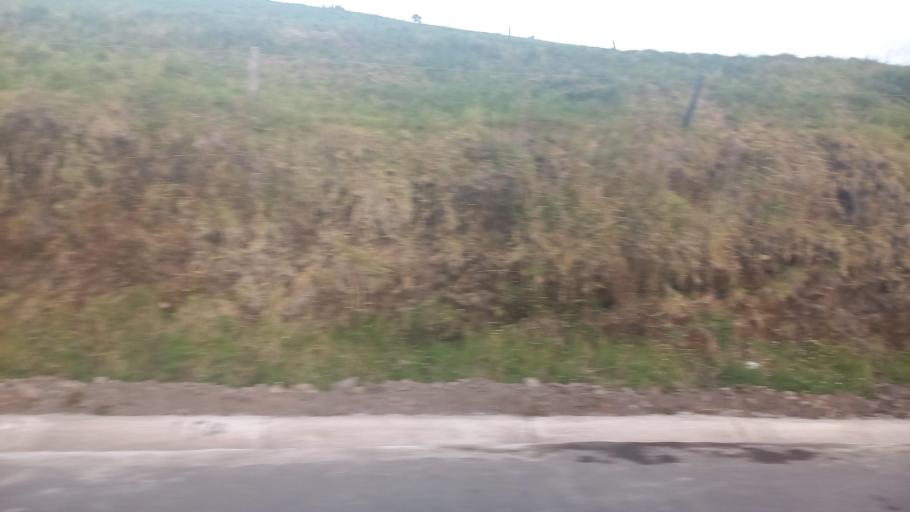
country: EC
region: Pichincha
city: Cayambe
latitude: 0.1203
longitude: -78.0777
